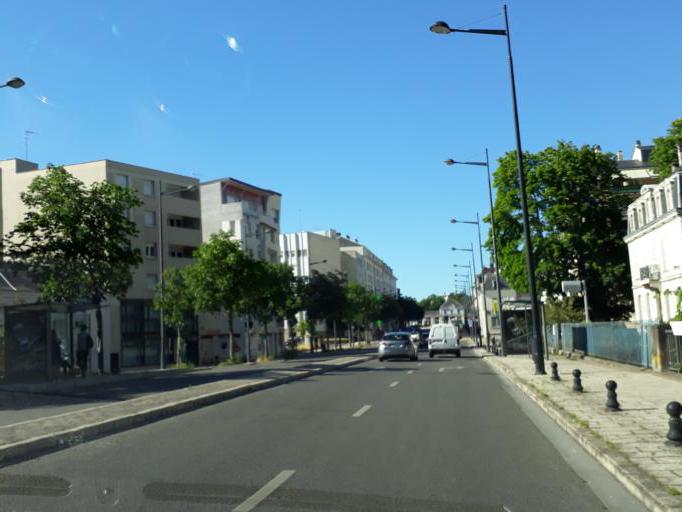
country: FR
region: Centre
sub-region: Departement du Cher
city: Bourges
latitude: 47.0911
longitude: 2.3937
